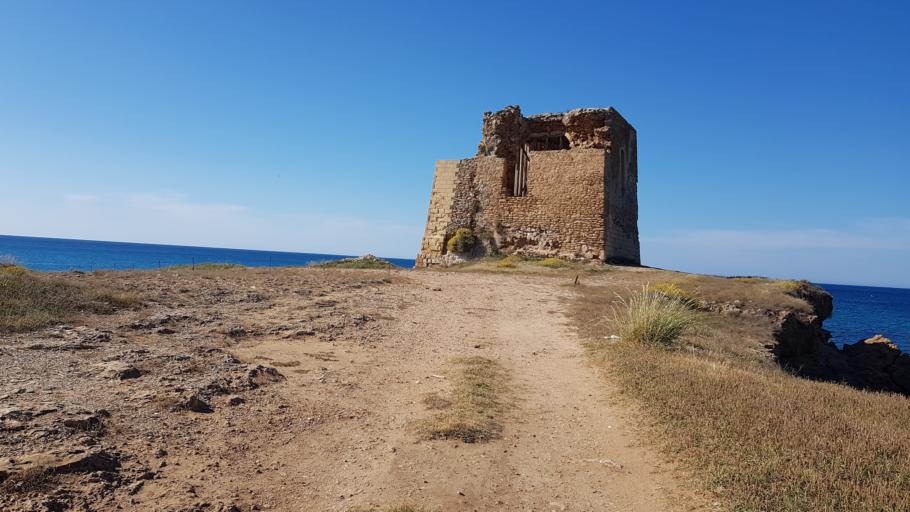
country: IT
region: Apulia
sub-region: Provincia di Brindisi
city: Brindisi
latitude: 40.6879
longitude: 17.8696
